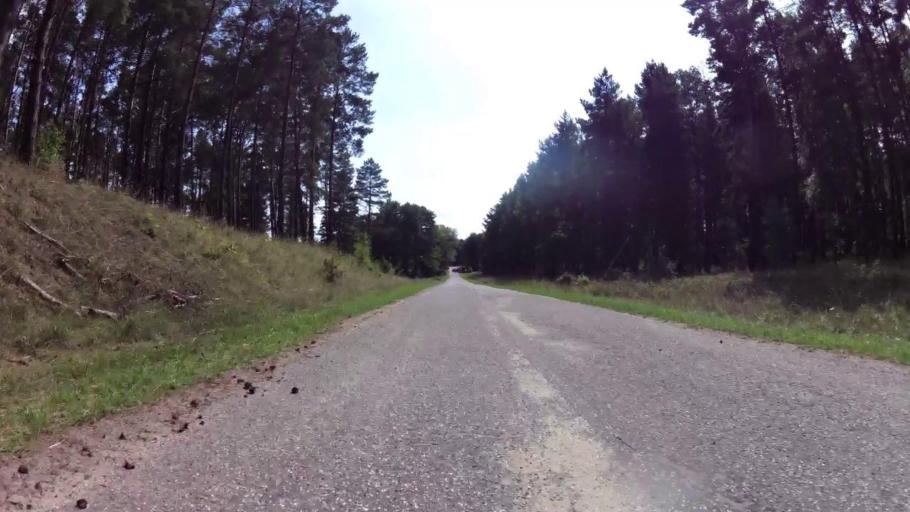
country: PL
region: West Pomeranian Voivodeship
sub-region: Powiat choszczenski
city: Drawno
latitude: 53.3199
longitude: 15.6876
